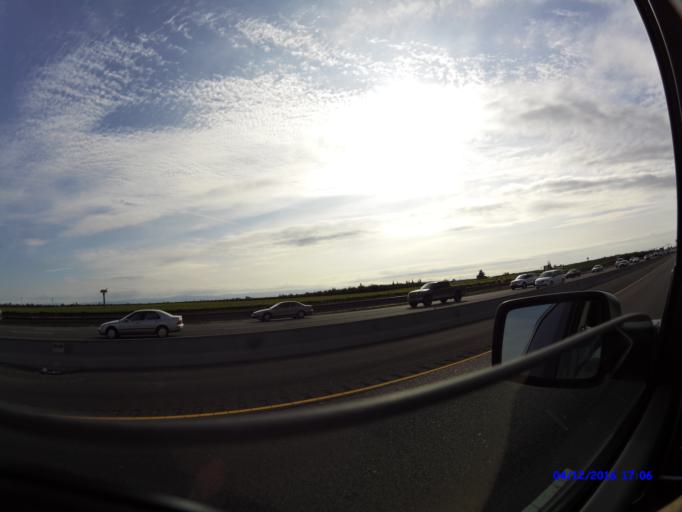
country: US
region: California
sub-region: San Joaquin County
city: Ripon
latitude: 37.7559
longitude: -121.1488
